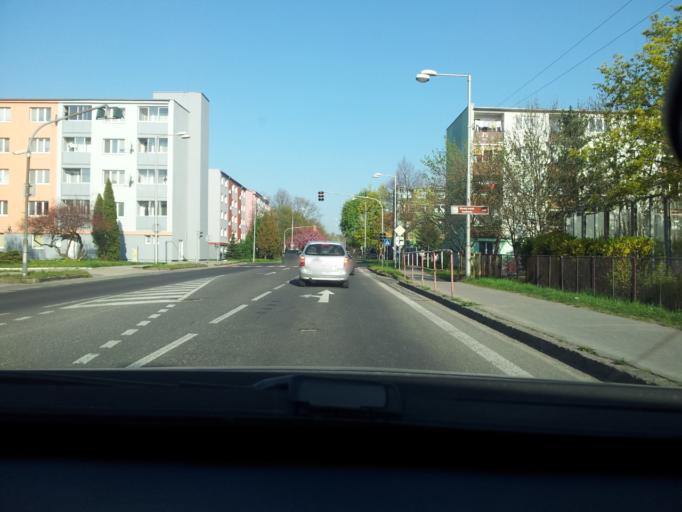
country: SK
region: Nitriansky
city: Zlate Moravce
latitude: 48.3833
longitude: 18.3881
